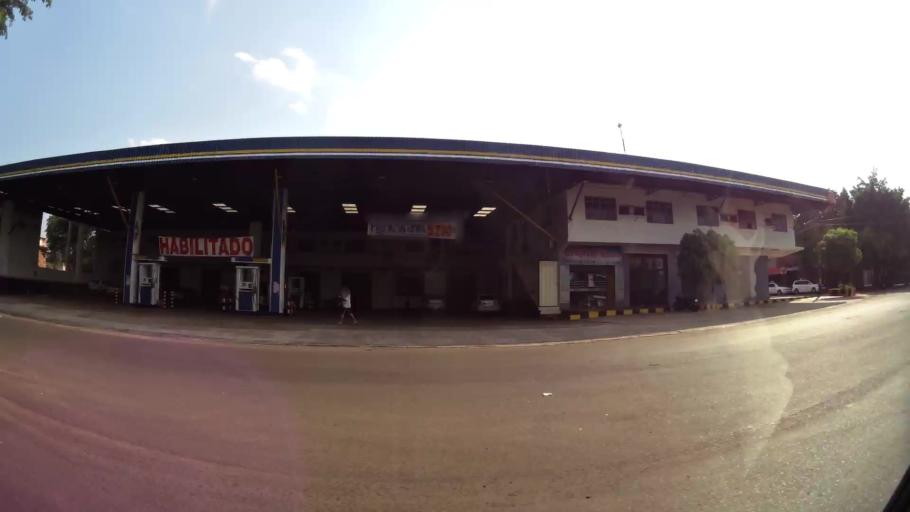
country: PY
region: Alto Parana
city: Presidente Franco
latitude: -25.5276
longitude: -54.6159
